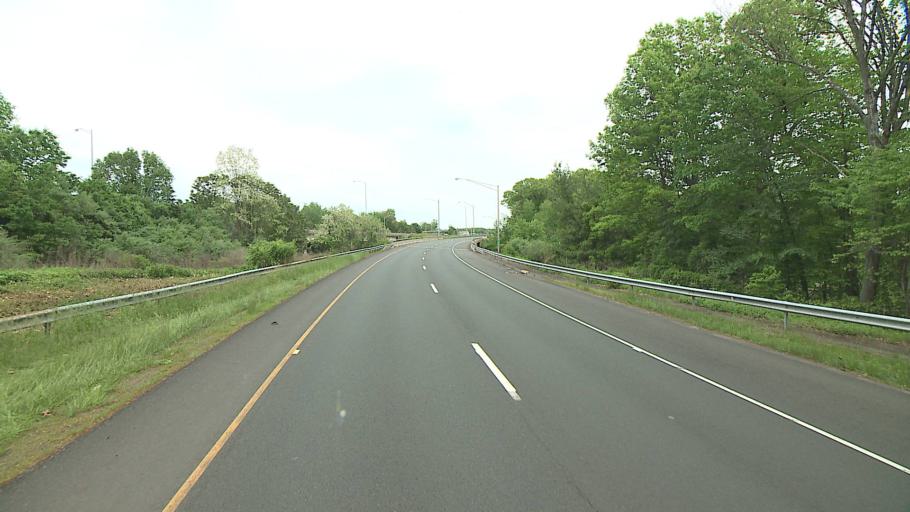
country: US
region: Connecticut
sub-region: Hartford County
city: East Hartford
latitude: 41.7733
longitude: -72.5781
